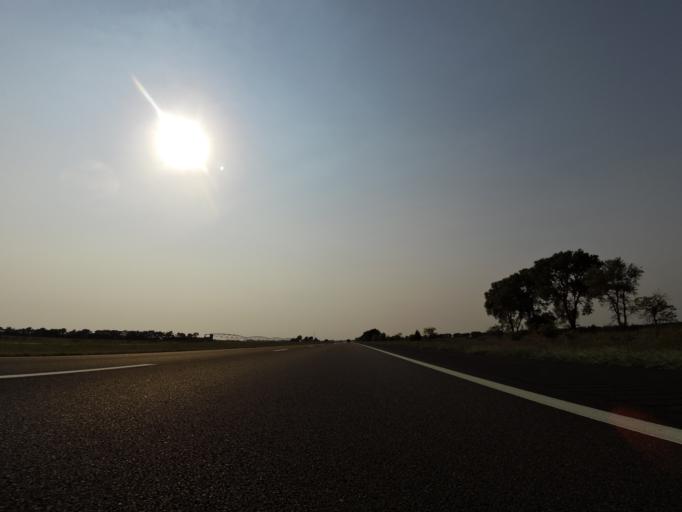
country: US
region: Kansas
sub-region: Reno County
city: Haven
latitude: 37.8876
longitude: -97.7407
